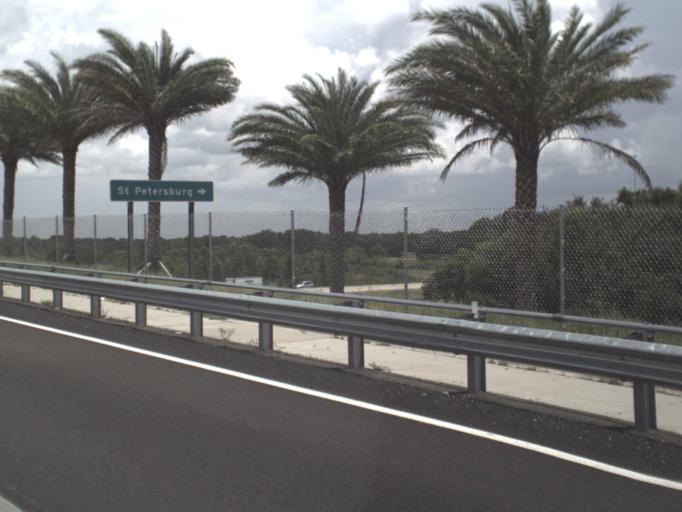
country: US
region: Florida
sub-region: Hillsborough County
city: East Lake-Orient Park
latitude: 27.9949
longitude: -82.3578
